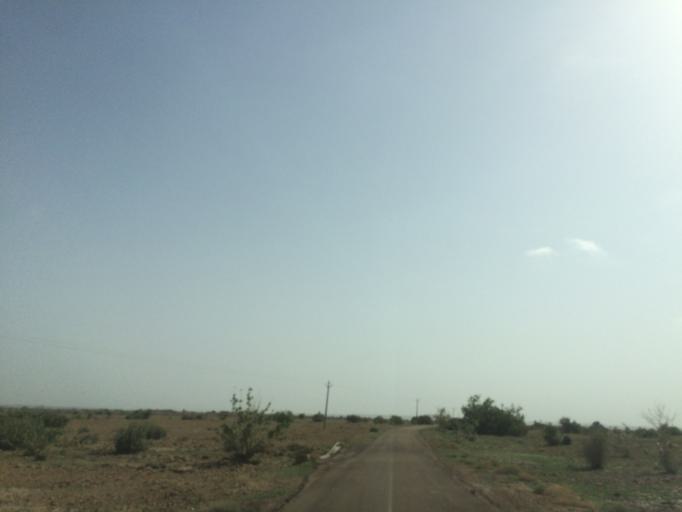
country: IN
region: Rajasthan
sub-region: Jaisalmer
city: Jaisalmer
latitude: 26.8540
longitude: 70.7576
